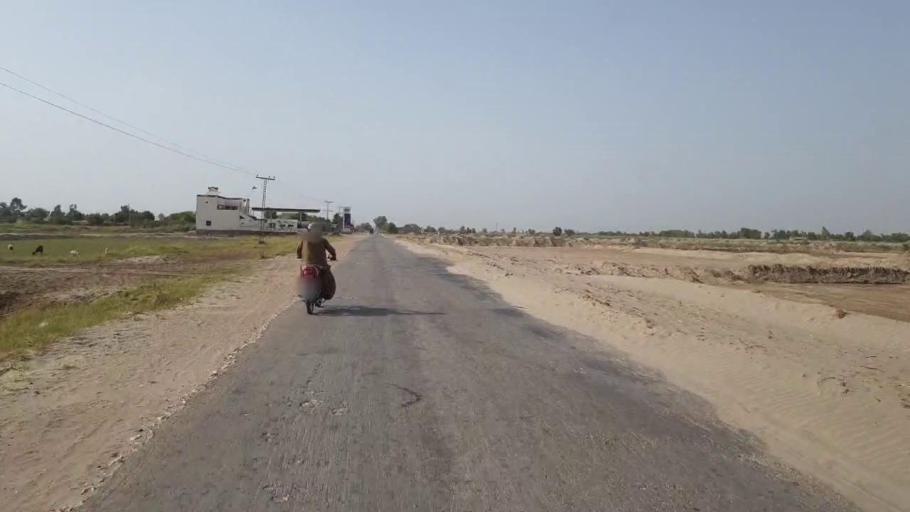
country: PK
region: Sindh
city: Sanghar
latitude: 26.2841
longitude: 68.9306
